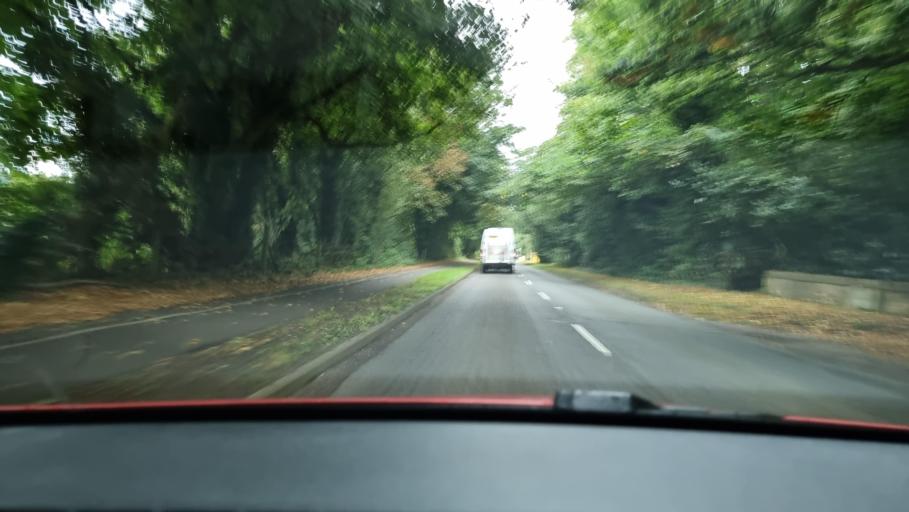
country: GB
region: England
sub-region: Hertfordshire
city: Tring
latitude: 51.7989
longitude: -0.6390
